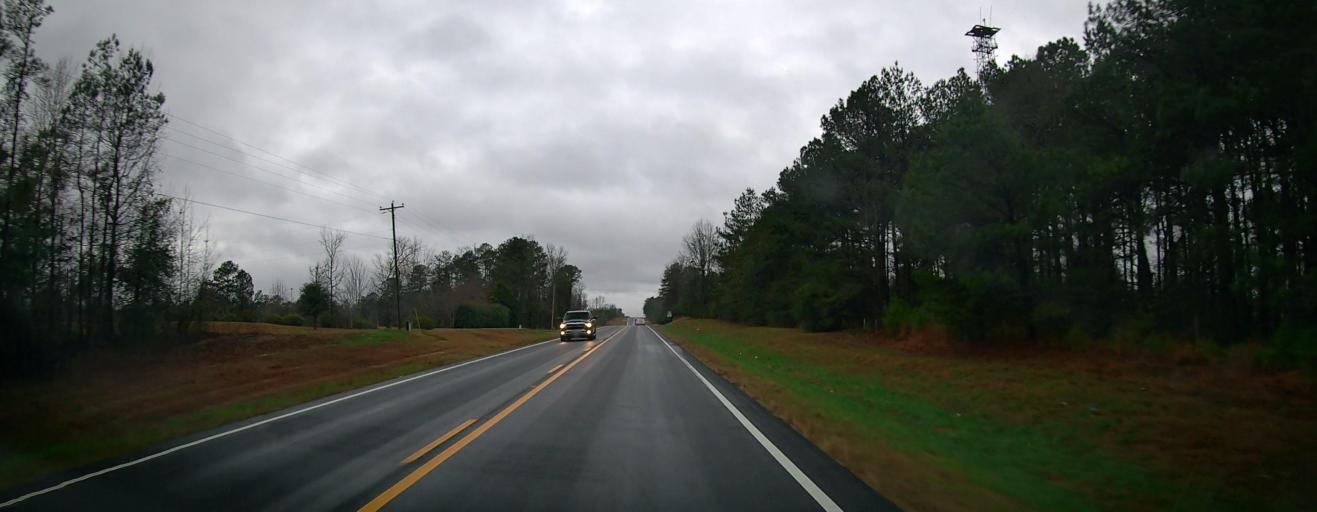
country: US
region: Alabama
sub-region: Bibb County
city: Centreville
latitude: 32.8113
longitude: -86.9287
